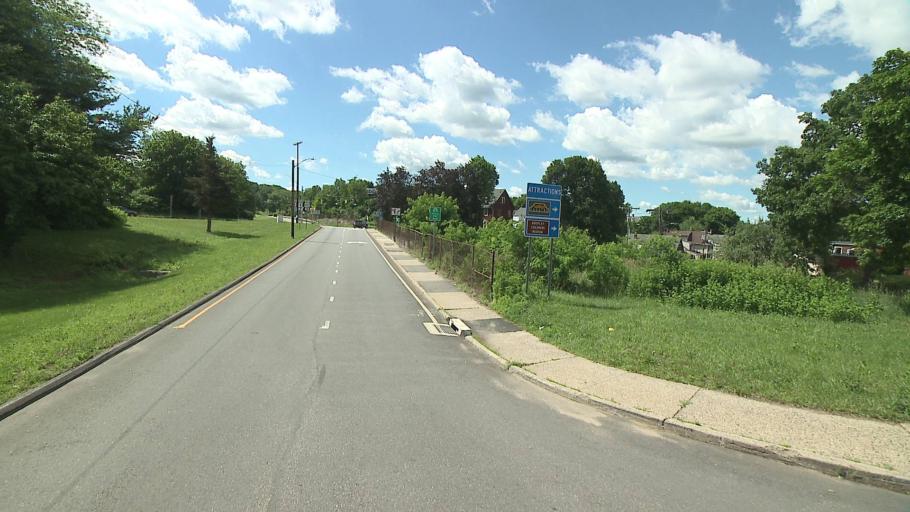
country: US
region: Connecticut
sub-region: Litchfield County
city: Torrington
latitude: 41.8064
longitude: -73.1142
